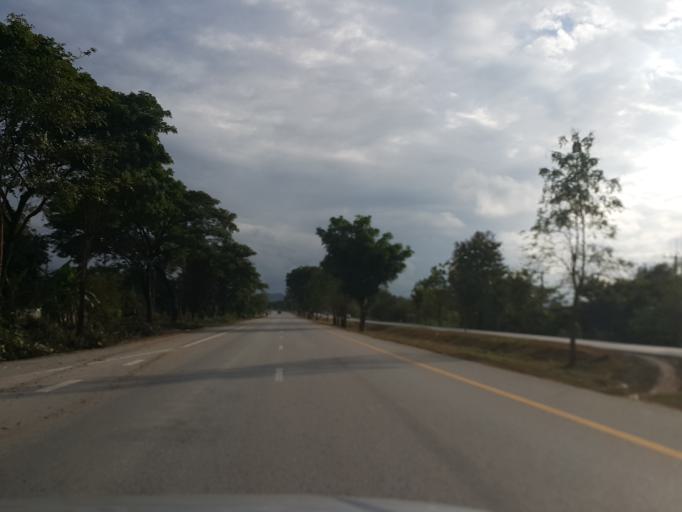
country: TH
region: Lampang
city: Ko Kha
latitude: 18.1630
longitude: 99.4047
